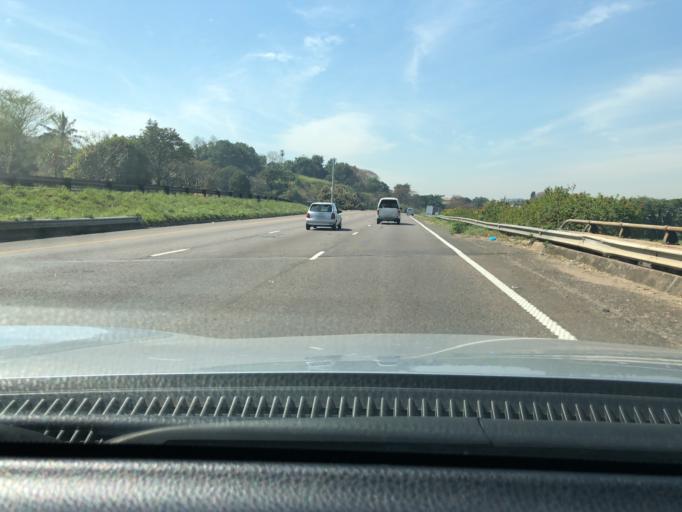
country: ZA
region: KwaZulu-Natal
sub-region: eThekwini Metropolitan Municipality
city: Berea
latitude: -29.8368
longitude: 30.8614
